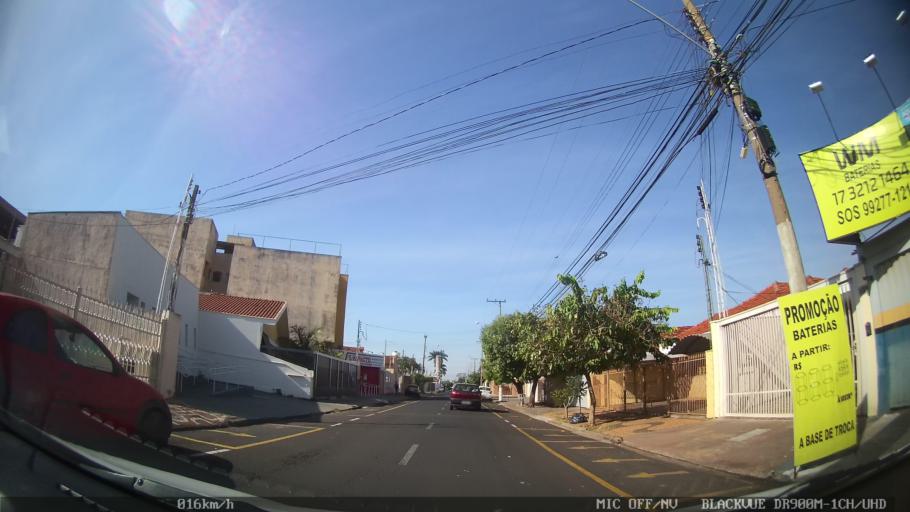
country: BR
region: Sao Paulo
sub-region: Sao Jose Do Rio Preto
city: Sao Jose do Rio Preto
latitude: -20.8080
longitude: -49.3939
